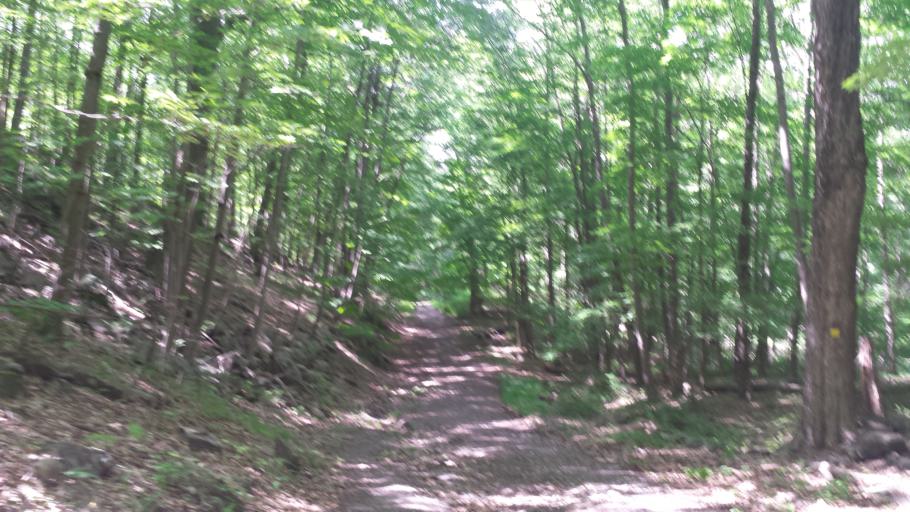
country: US
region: New York
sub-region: Westchester County
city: Pound Ridge
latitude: 41.2443
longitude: -73.5894
